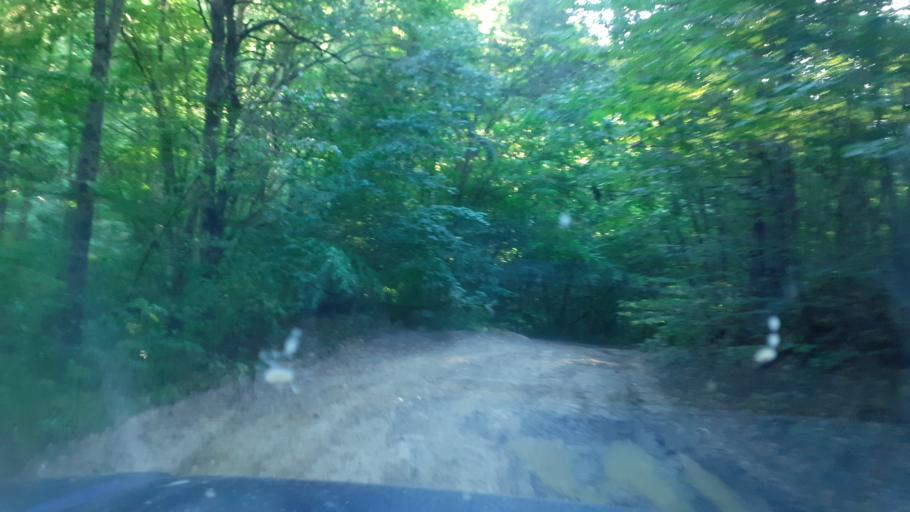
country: RU
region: Krasnodarskiy
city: Pshada
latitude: 44.6561
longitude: 38.4531
